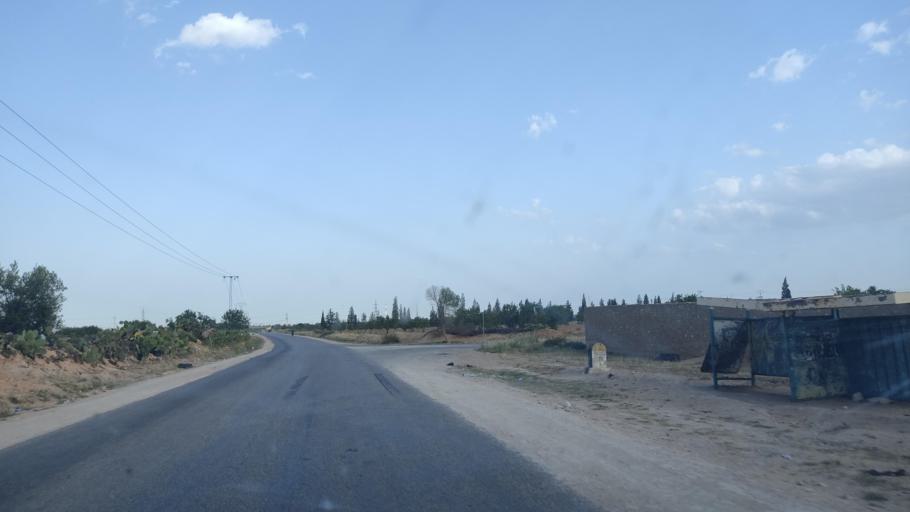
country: TN
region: Safaqis
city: Sfax
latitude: 34.8396
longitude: 10.6250
